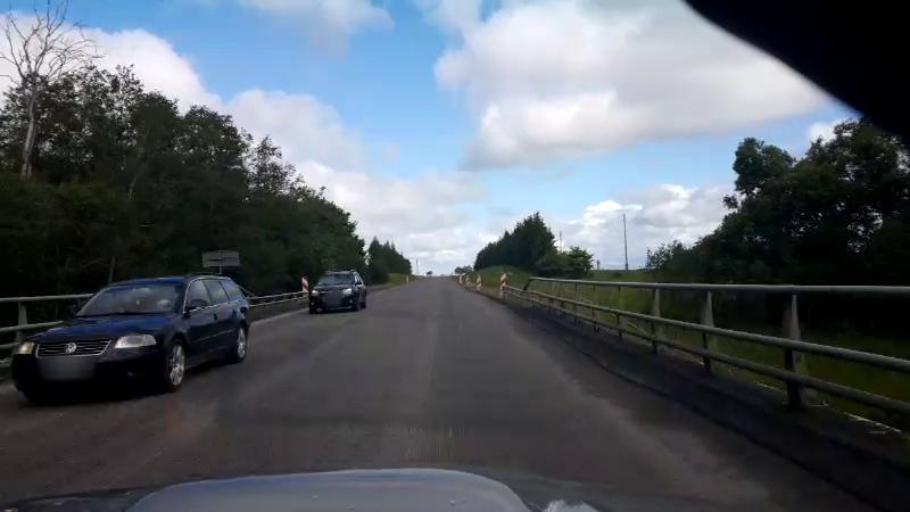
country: LV
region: Bauskas Rajons
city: Bauska
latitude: 56.3283
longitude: 24.3052
